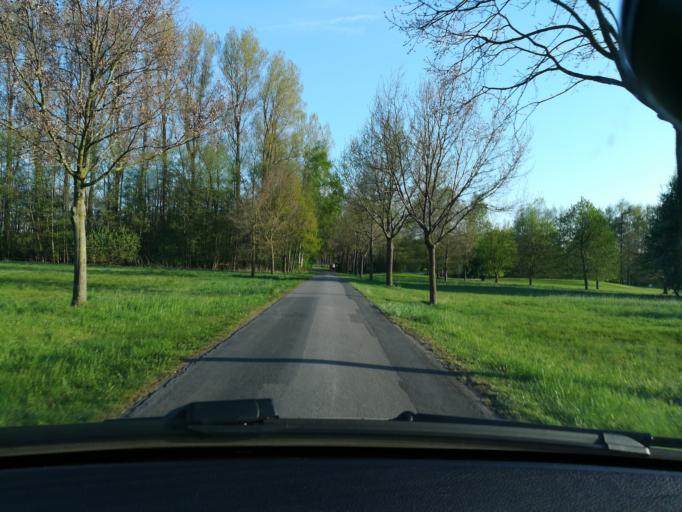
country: DE
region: North Rhine-Westphalia
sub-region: Regierungsbezirk Munster
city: Sassenberg
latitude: 52.0185
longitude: 8.0930
